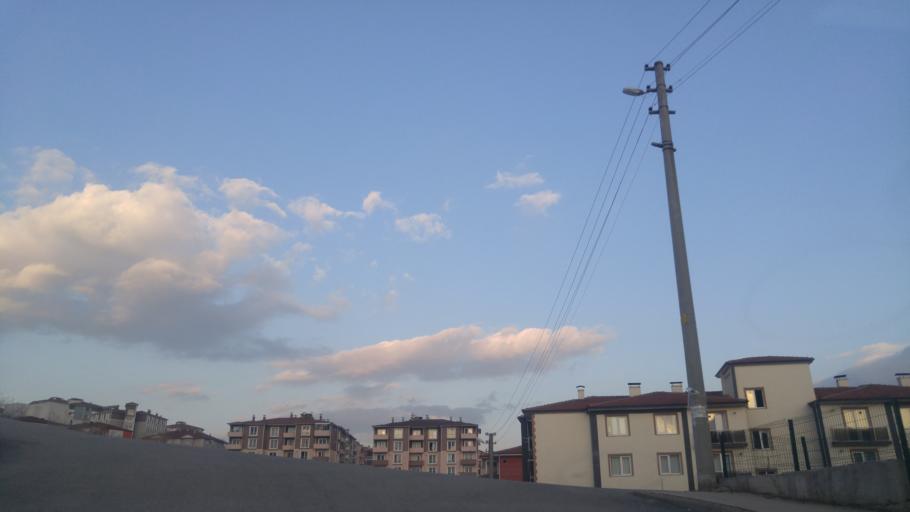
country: TR
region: Karabuk
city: Karabuk
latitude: 41.2210
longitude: 32.6655
